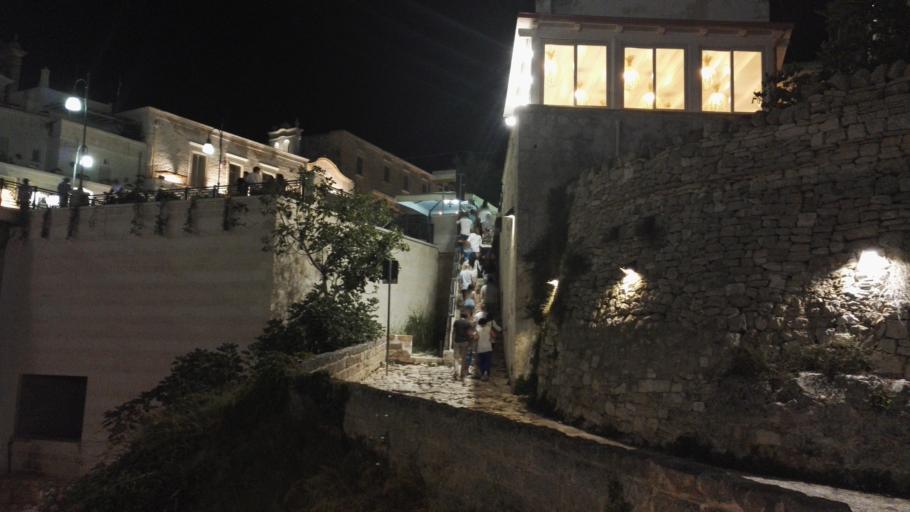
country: IT
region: Apulia
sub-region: Provincia di Bari
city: Polignano a Mare
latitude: 40.9953
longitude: 17.2179
